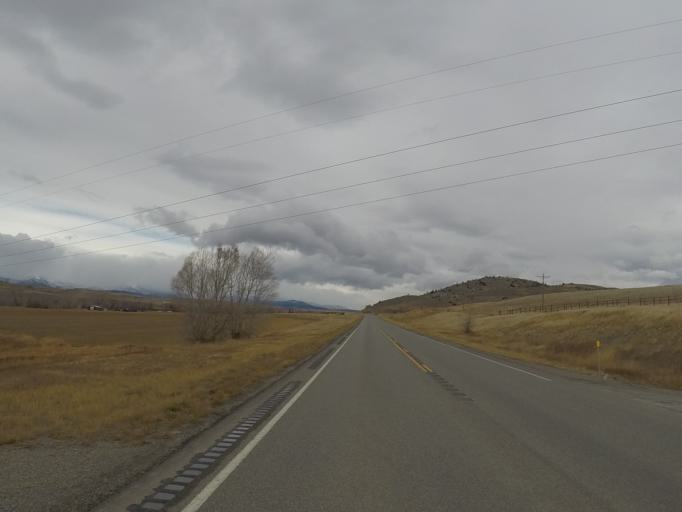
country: US
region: Montana
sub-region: Sweet Grass County
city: Big Timber
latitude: 45.8712
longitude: -109.9462
